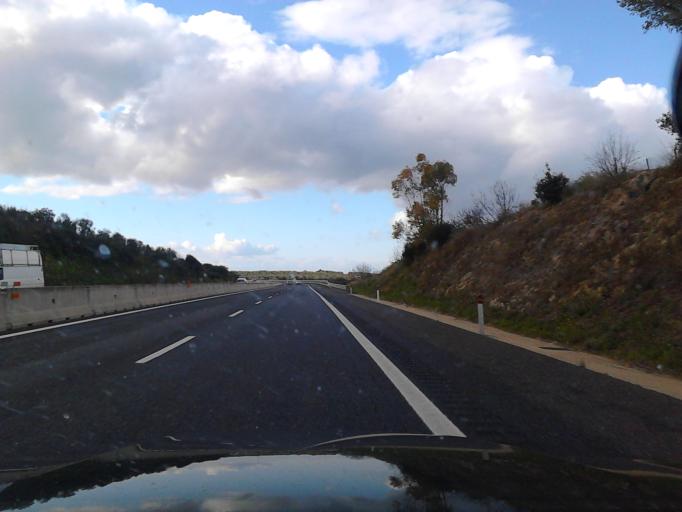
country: IT
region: Apulia
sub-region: Provincia di Barletta - Andria - Trani
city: Andria
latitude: 41.2619
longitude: 16.2565
